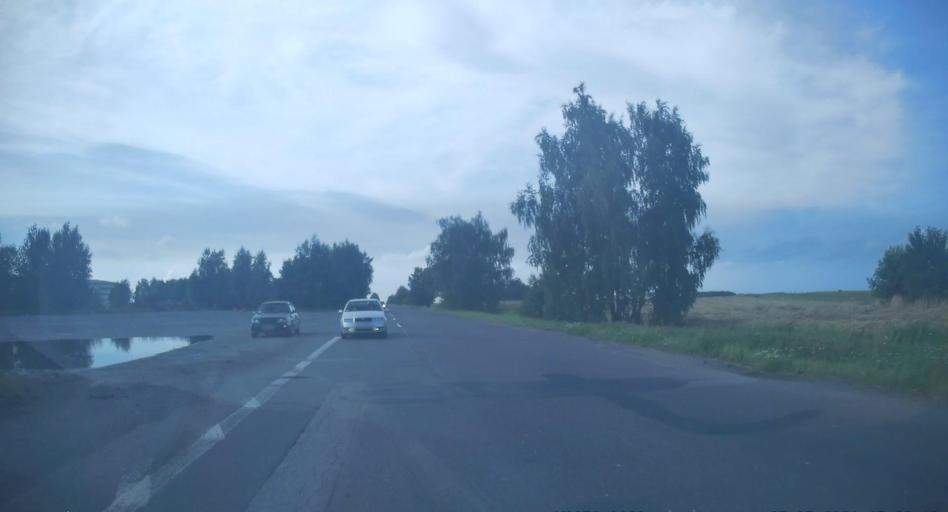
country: PL
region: Lodz Voivodeship
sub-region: Powiat tomaszowski
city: Rzeczyca
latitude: 51.6477
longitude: 20.2820
